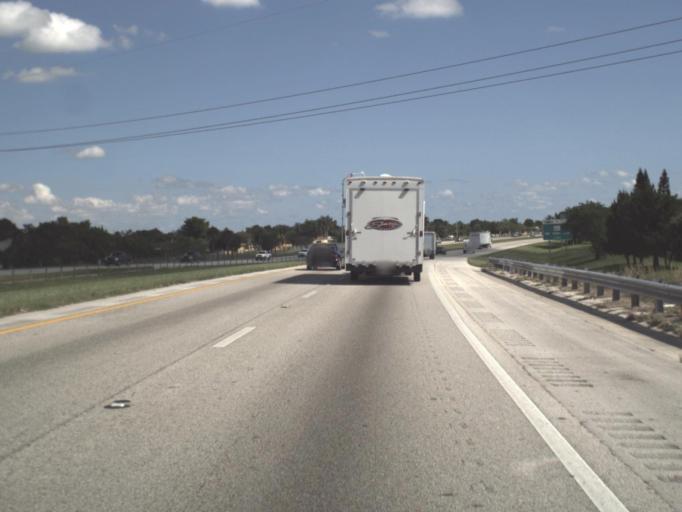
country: US
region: Florida
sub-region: Miami-Dade County
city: Princeton
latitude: 25.5263
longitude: -80.3969
